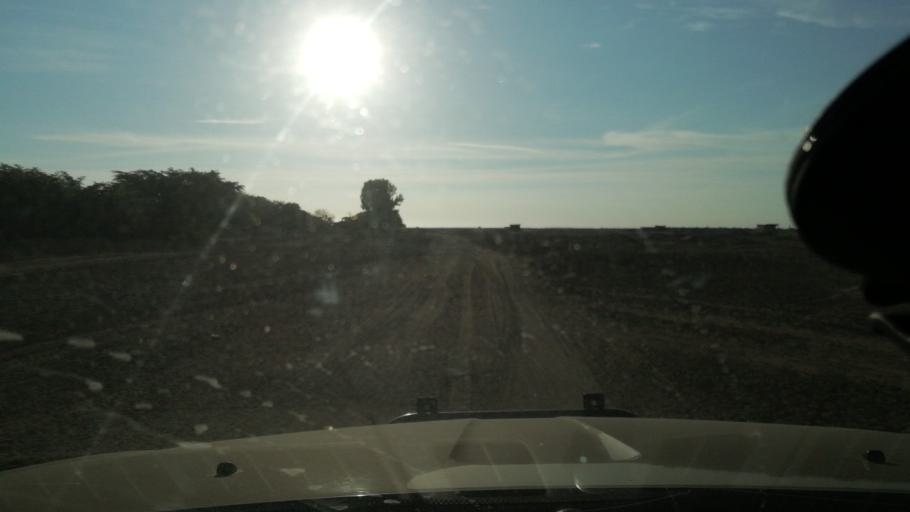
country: PE
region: Ica
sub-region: Provincia de Chincha
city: San Pedro
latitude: -13.3308
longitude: -76.1828
